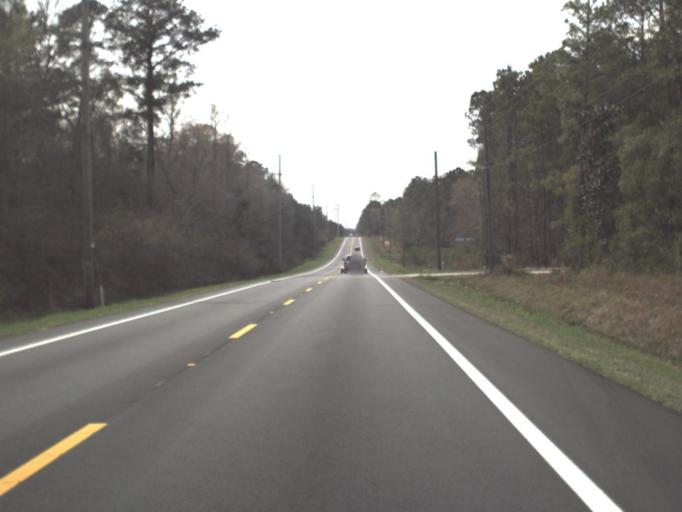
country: US
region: Florida
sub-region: Gadsden County
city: Midway
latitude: 30.3948
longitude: -84.6120
